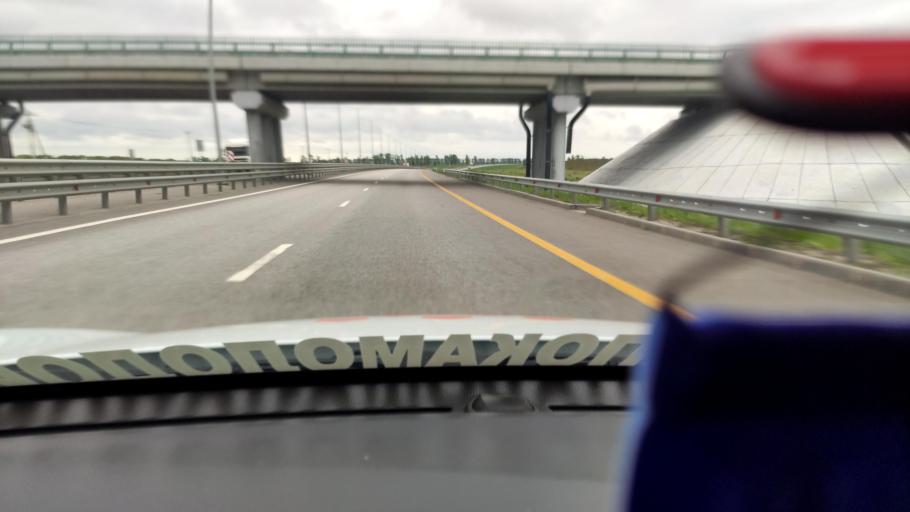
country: RU
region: Voronezj
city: Podkletnoye
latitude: 51.5346
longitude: 39.5065
